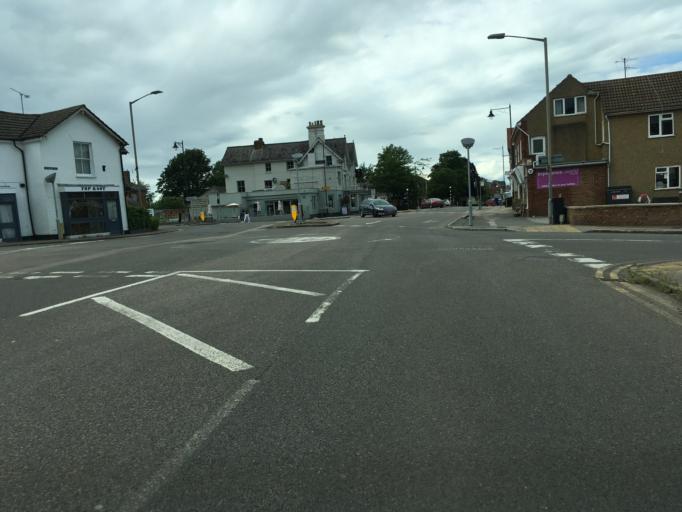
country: GB
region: England
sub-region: Milton Keynes
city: Woburn Sands
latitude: 52.0101
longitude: -0.6460
